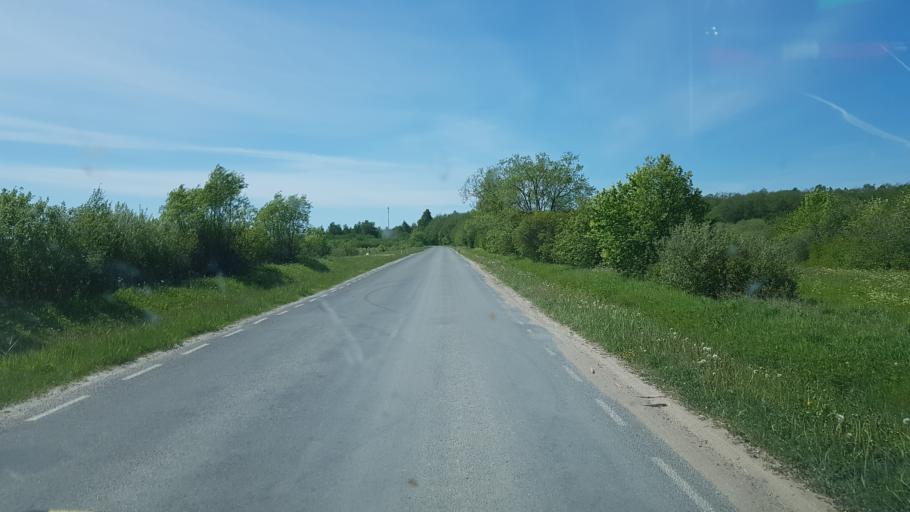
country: EE
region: Saare
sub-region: Kuressaare linn
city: Kuressaare
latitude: 58.2817
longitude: 22.5044
